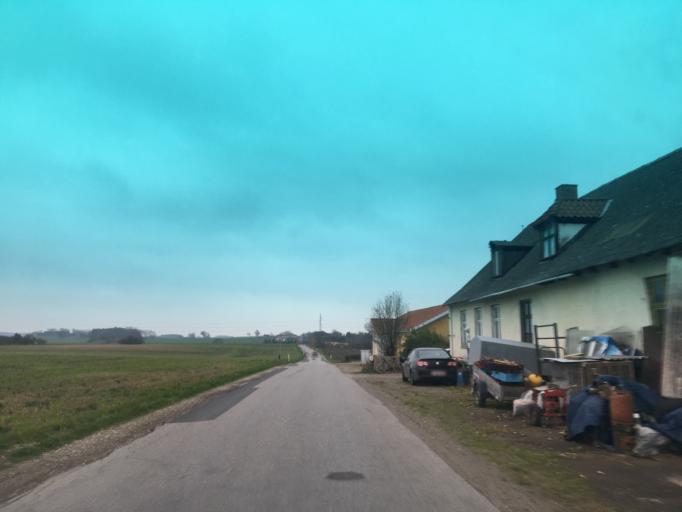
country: DK
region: Zealand
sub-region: Slagelse Kommune
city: Skaelskor
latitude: 55.2366
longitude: 11.4241
